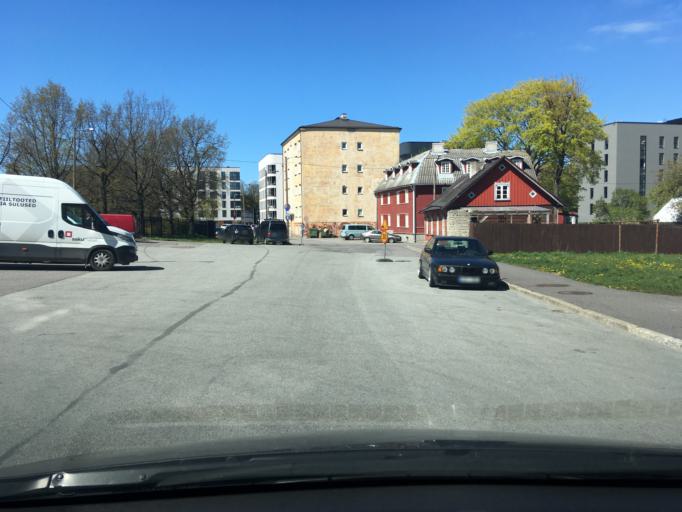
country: EE
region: Harju
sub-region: Tallinna linn
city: Tallinn
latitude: 59.4268
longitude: 24.7666
